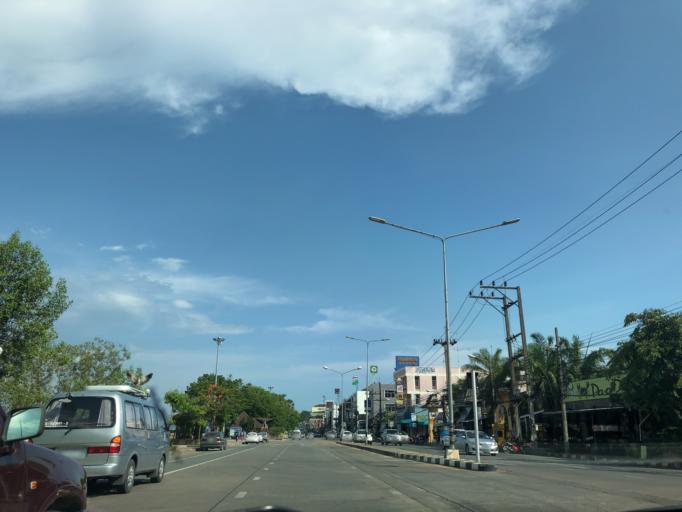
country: TH
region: Krabi
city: Krabi
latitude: 8.0679
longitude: 98.9169
